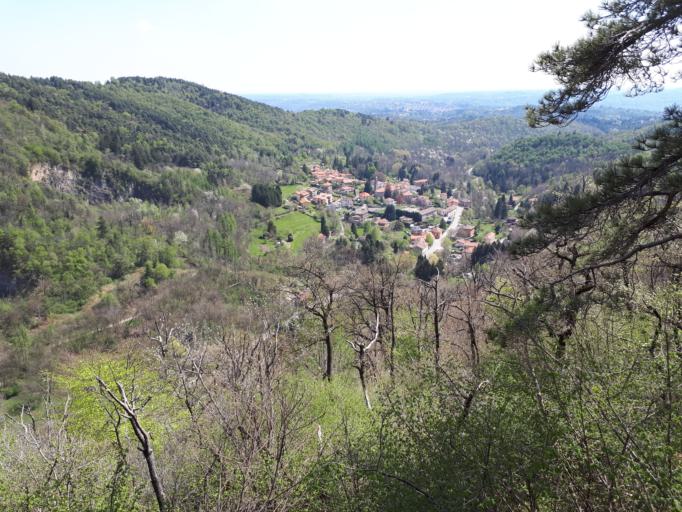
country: IT
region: Lombardy
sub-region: Provincia di Varese
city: Brinzio
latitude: 45.8723
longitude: 8.8019
